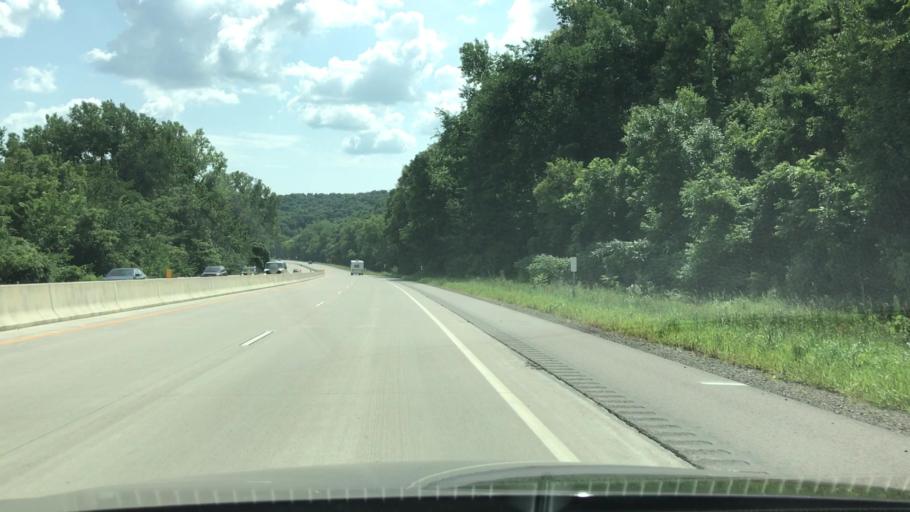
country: US
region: Minnesota
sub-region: Nicollet County
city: Saint Peter
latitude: 44.2684
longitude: -94.0227
